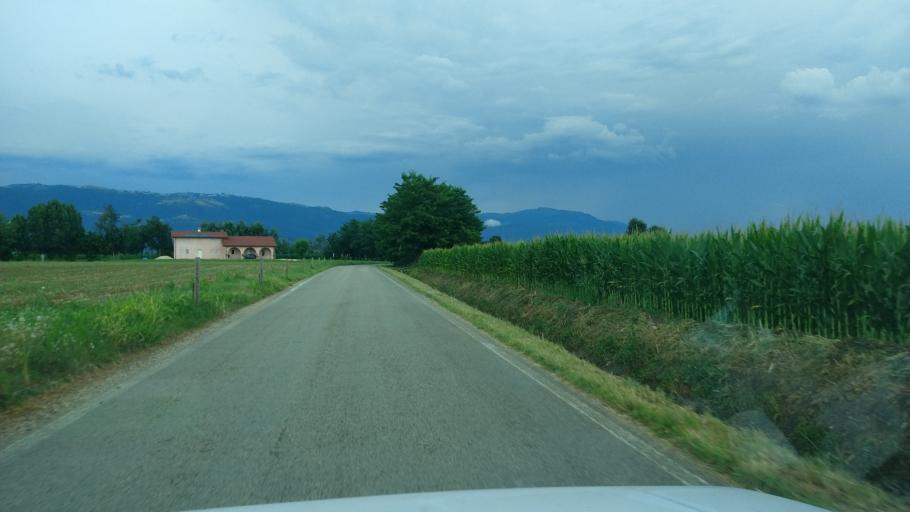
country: IT
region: Veneto
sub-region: Provincia di Vicenza
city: Schiavon
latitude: 45.7095
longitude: 11.6567
